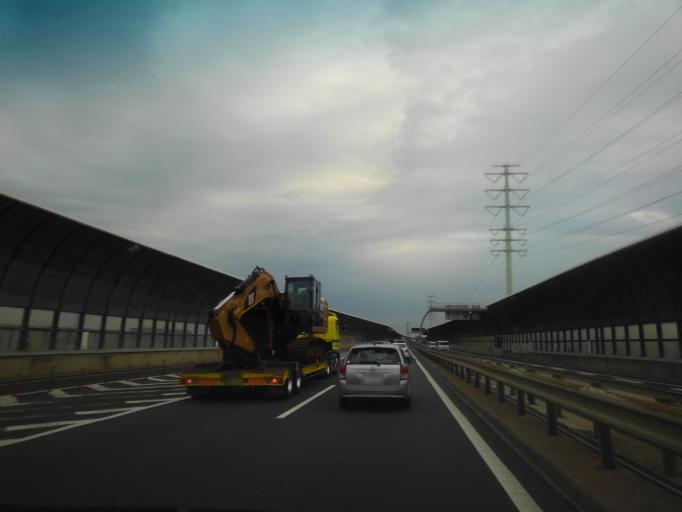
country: JP
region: Saitama
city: Shimotoda
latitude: 35.8389
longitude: 139.6783
